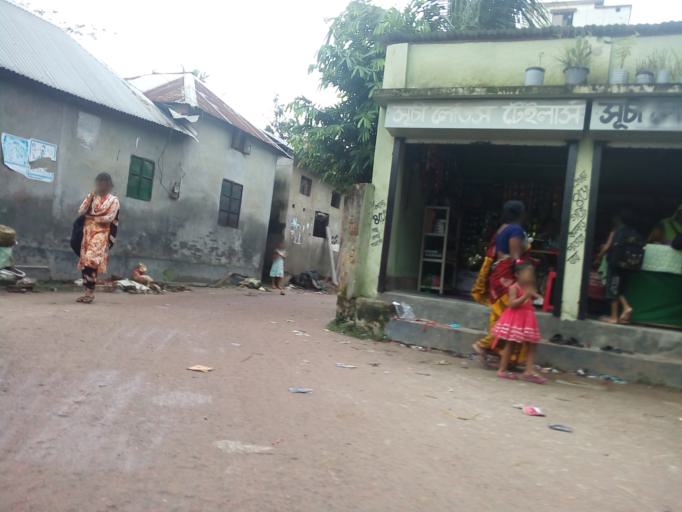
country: BD
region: Dhaka
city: Tungi
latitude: 23.8429
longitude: 90.2513
